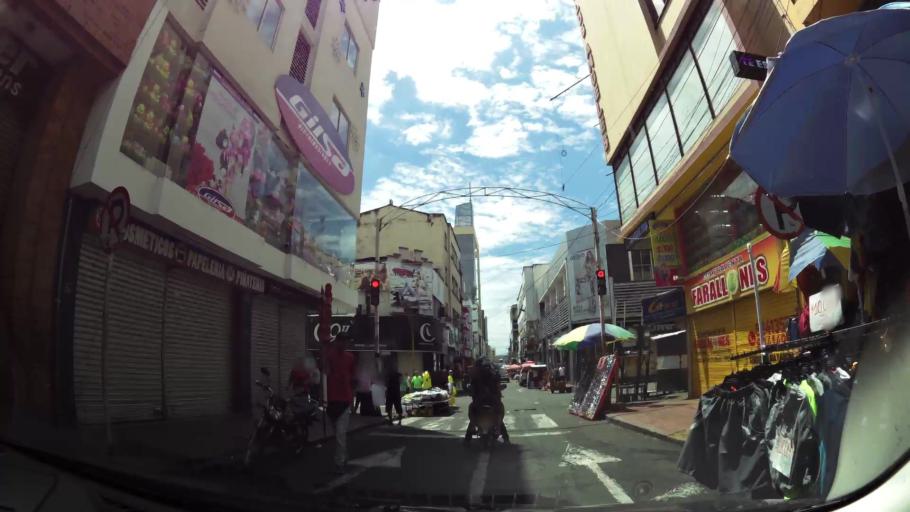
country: CO
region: Valle del Cauca
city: Cali
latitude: 3.4519
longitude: -76.5299
